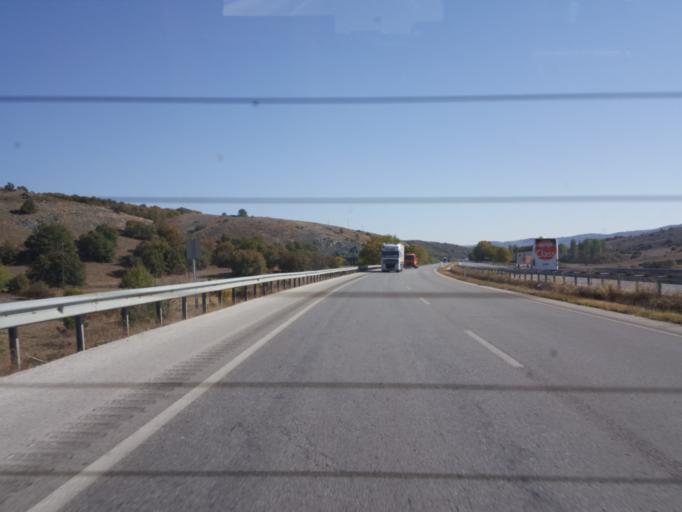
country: TR
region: Corum
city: Alaca
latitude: 40.3123
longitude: 34.6619
